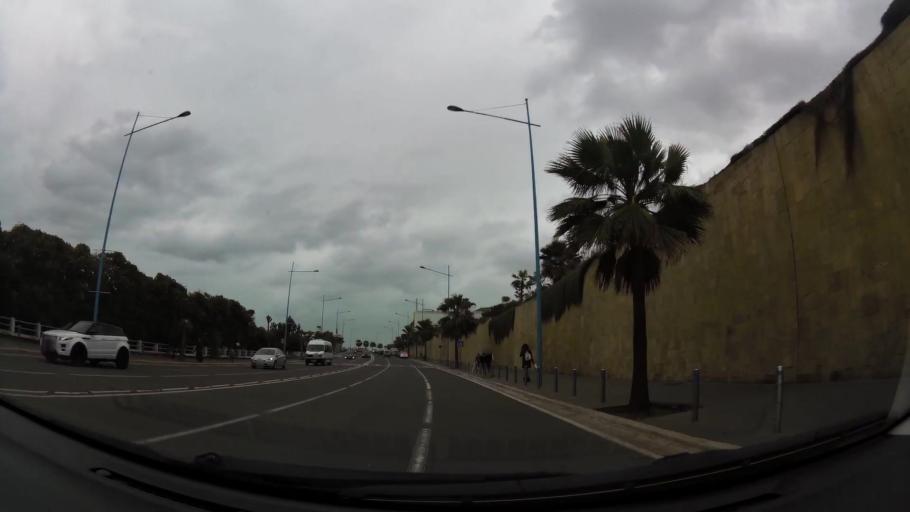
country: MA
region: Grand Casablanca
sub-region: Casablanca
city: Casablanca
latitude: 33.5958
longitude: -7.6671
